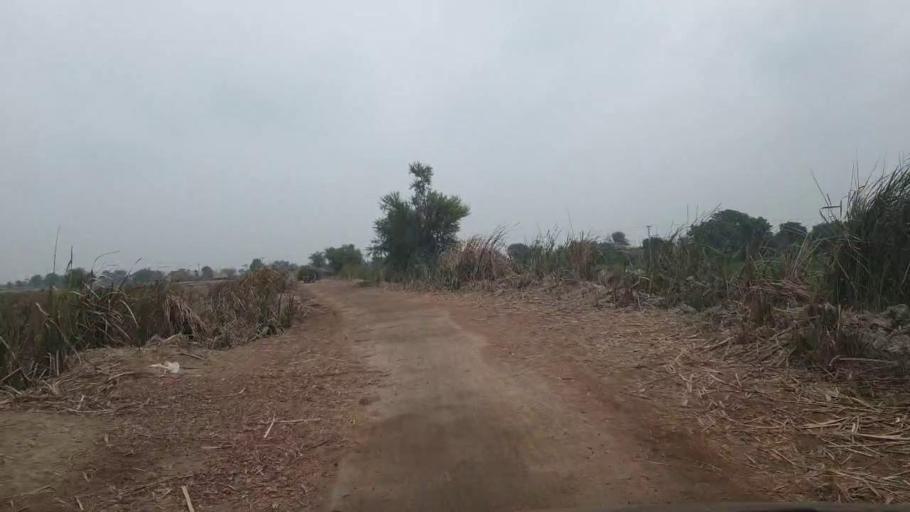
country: PK
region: Sindh
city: Tando Adam
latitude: 25.8533
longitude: 68.7018
